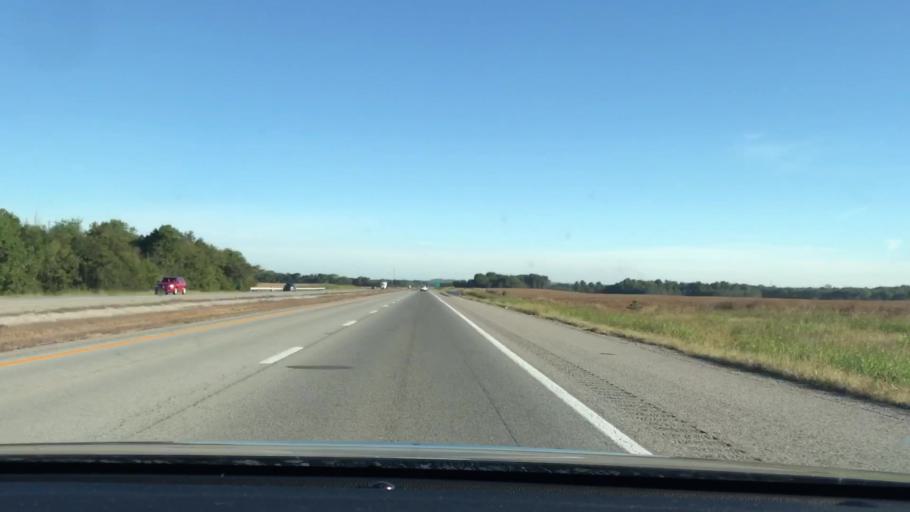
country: US
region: Kentucky
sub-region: Christian County
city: Hopkinsville
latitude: 36.7824
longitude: -87.4970
